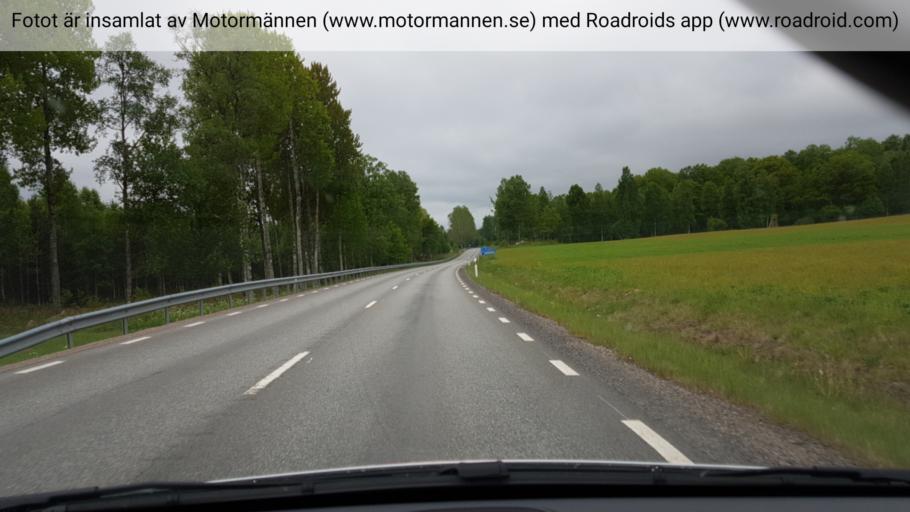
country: SE
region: Joenkoeping
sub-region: Mullsjo Kommun
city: Mullsjoe
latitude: 57.8404
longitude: 13.8540
